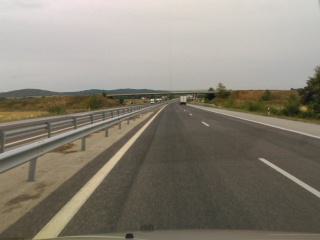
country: BG
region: Stara Zagora
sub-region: Obshtina Nikolaevo
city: Elkhovo
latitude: 42.3110
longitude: 25.5261
